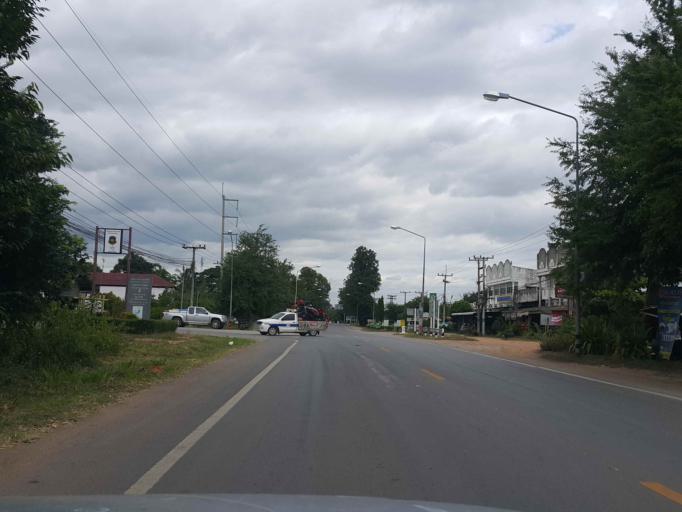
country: TH
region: Lamphun
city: Thung Hua Chang
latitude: 17.9925
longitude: 98.8758
